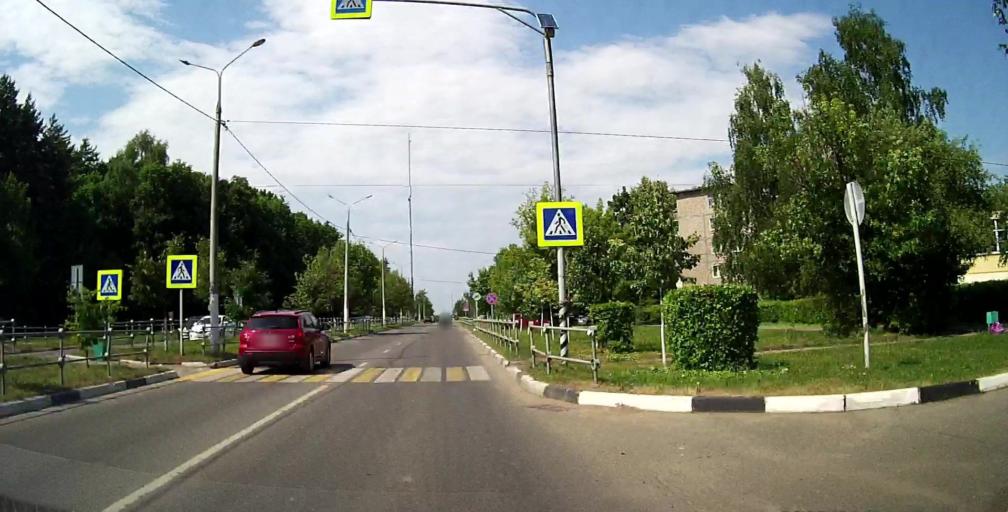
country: RU
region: Moskovskaya
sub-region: Podol'skiy Rayon
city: Podol'sk
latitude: 55.4146
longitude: 37.5219
